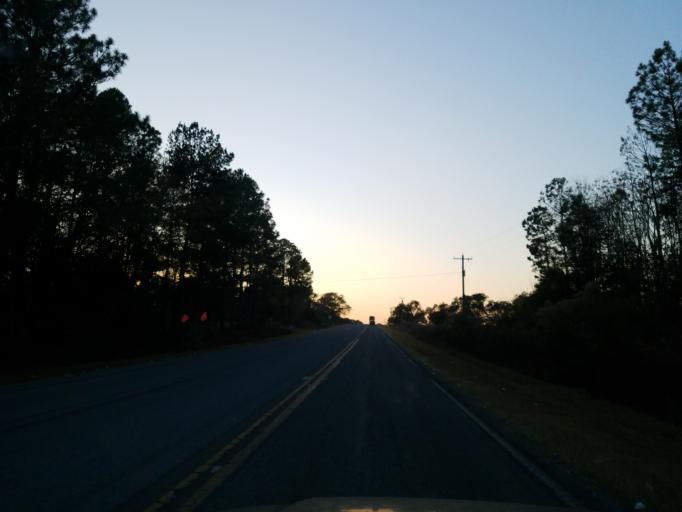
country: US
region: Georgia
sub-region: Ben Hill County
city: Fitzgerald
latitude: 31.7198
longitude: -83.3912
